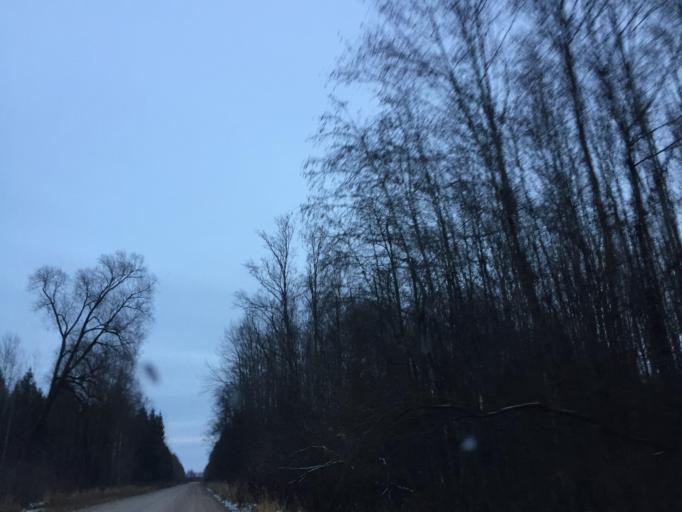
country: LV
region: Burtnieki
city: Matisi
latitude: 57.6297
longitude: 25.1513
